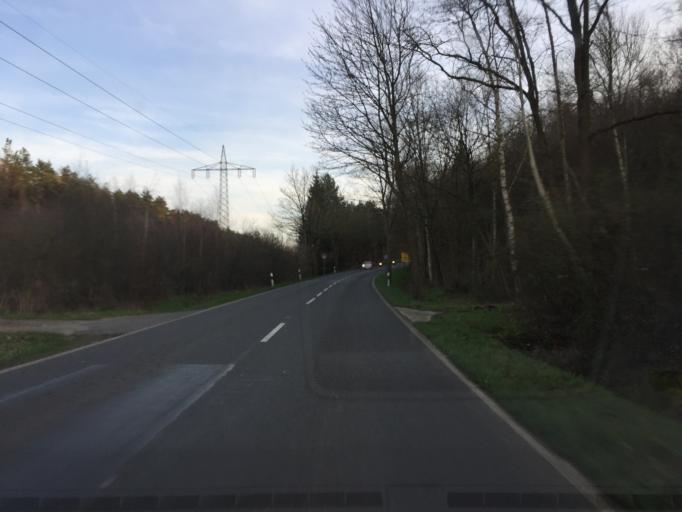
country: DE
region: Lower Saxony
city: Neustadt am Rubenberge
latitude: 52.4928
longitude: 9.4889
